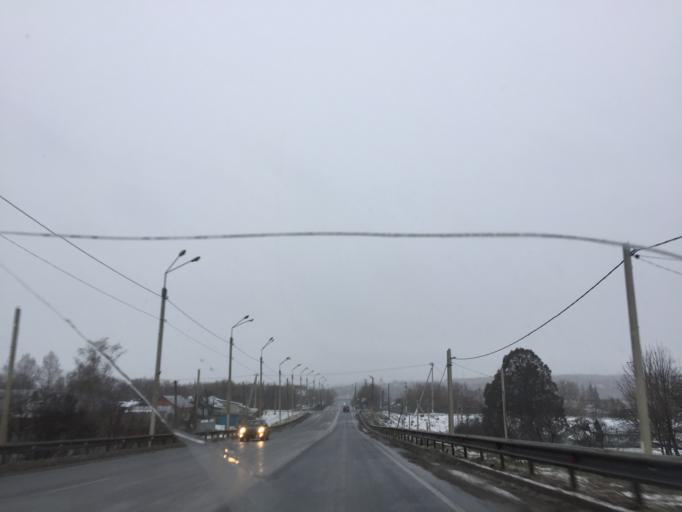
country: RU
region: Tula
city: Plavsk
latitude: 53.7186
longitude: 37.2981
